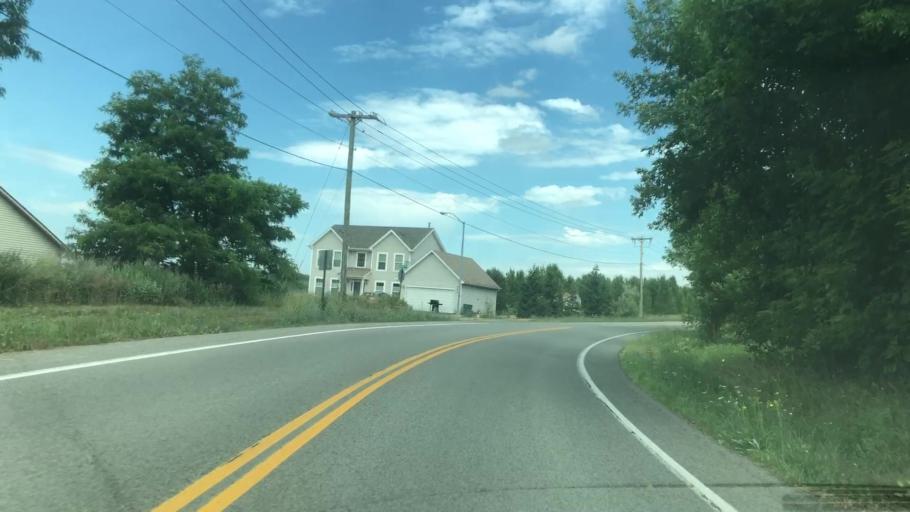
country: US
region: New York
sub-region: Wayne County
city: Macedon
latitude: 43.1236
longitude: -77.3530
